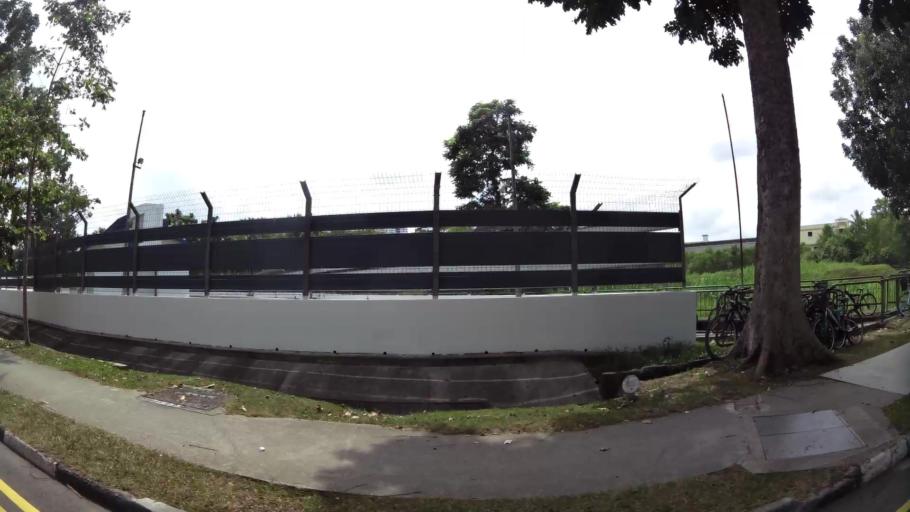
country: MY
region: Johor
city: Johor Bahru
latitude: 1.4074
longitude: 103.7553
